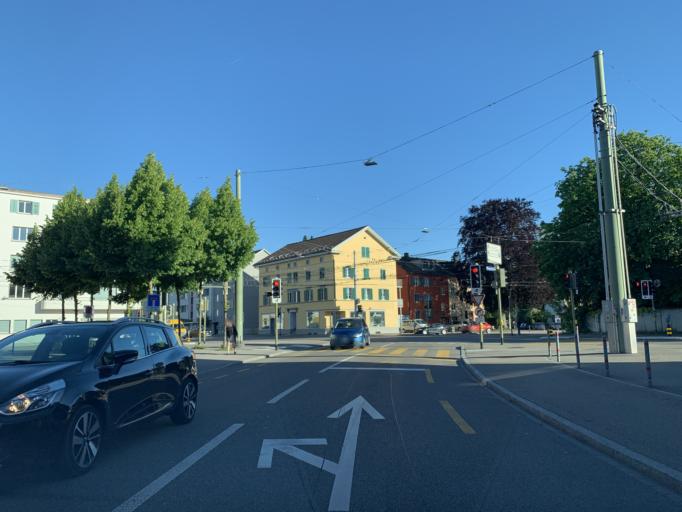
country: CH
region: Zurich
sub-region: Bezirk Winterthur
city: Mattenbach (Kreis 7) / Deutweg
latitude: 47.4943
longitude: 8.7411
